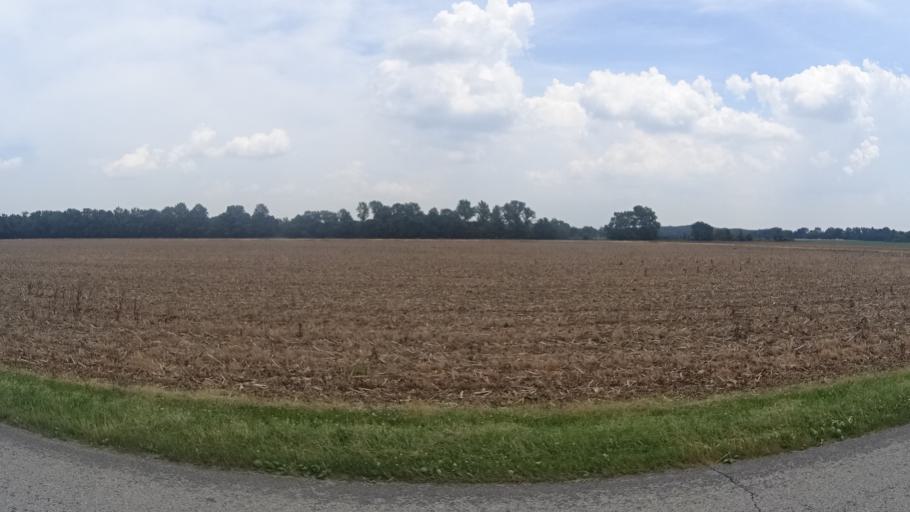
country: US
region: Ohio
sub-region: Huron County
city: Monroeville
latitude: 41.2990
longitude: -82.6719
